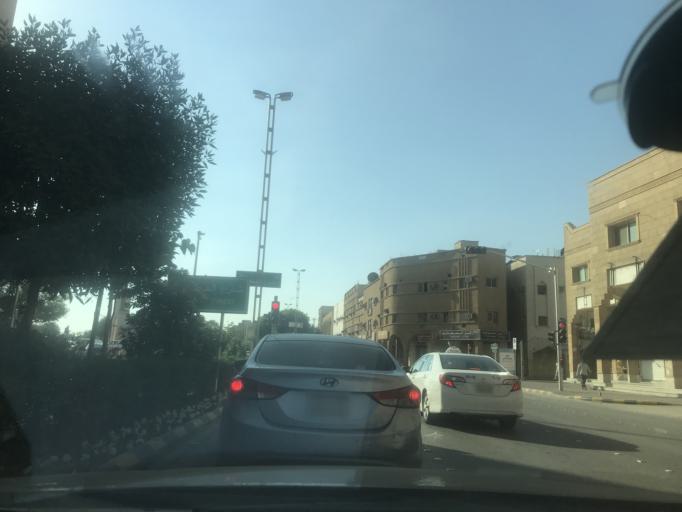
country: SA
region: Ar Riyad
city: Riyadh
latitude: 24.6312
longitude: 46.7078
